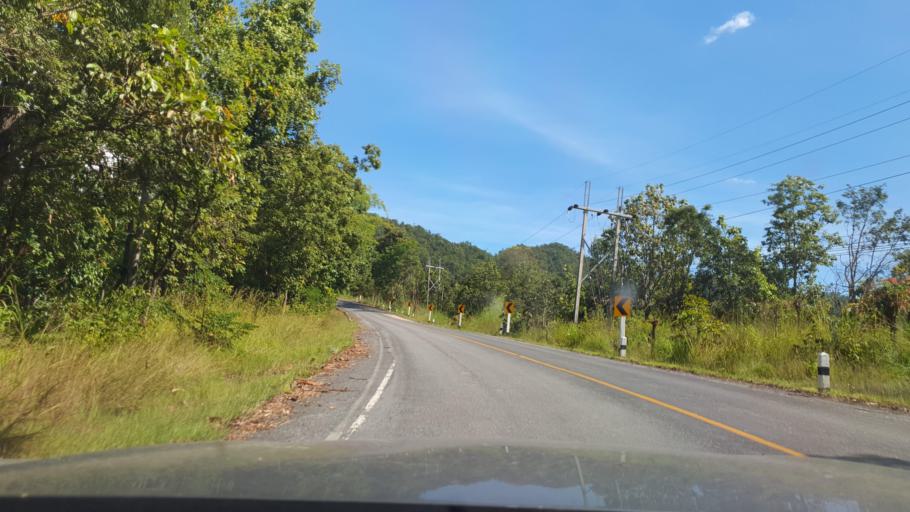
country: TH
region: Chiang Mai
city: Phrao
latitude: 19.3592
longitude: 99.2635
